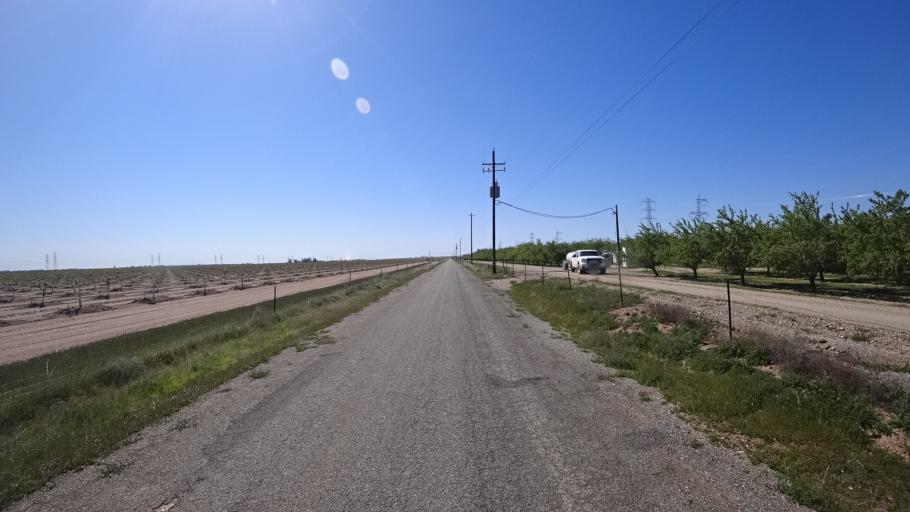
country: US
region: California
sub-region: Glenn County
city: Orland
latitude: 39.6638
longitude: -122.2719
